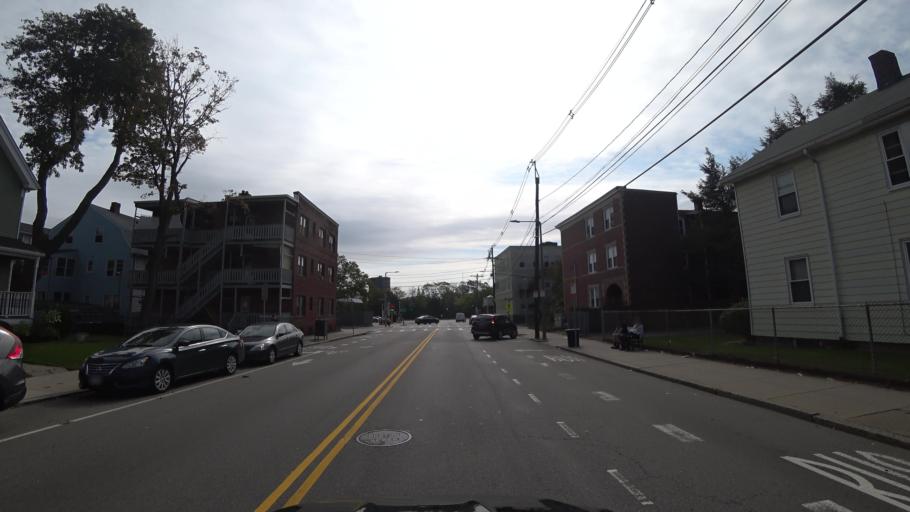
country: US
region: Massachusetts
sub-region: Middlesex County
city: Cambridge
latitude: 42.3588
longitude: -71.1271
